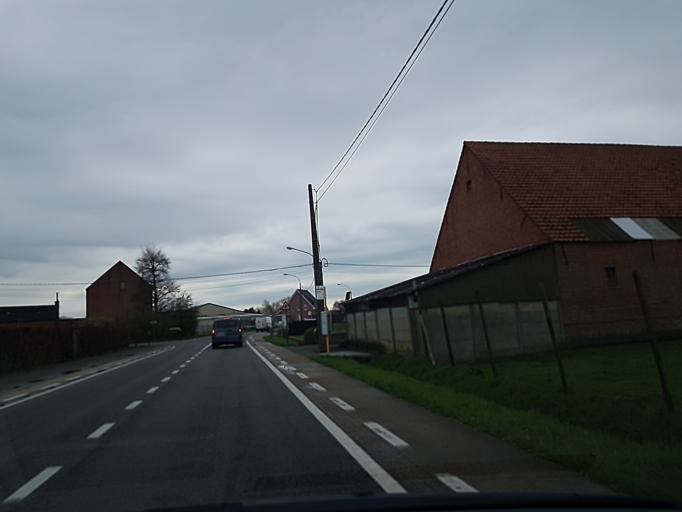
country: BE
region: Flanders
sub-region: Provincie Antwerpen
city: Ranst
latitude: 51.1893
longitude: 4.6045
